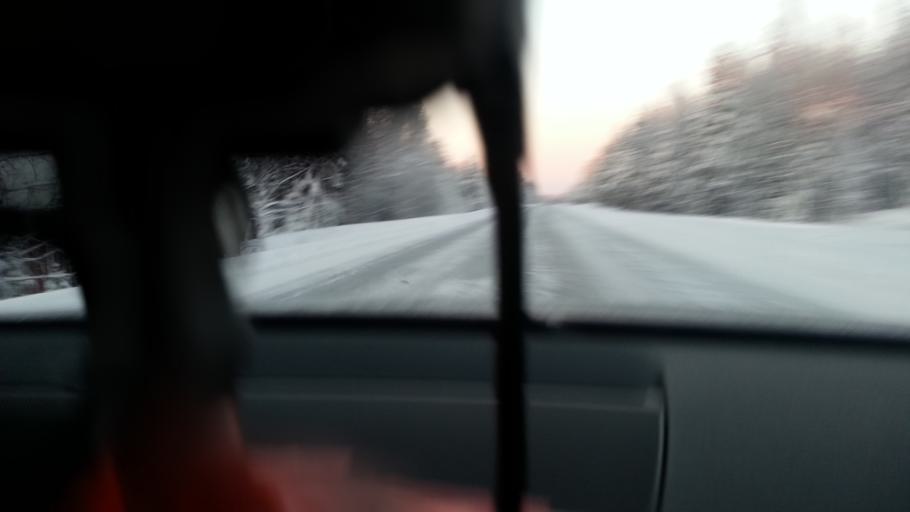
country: FI
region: Lapland
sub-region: Tunturi-Lappi
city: Kittilae
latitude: 67.2190
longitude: 24.9239
